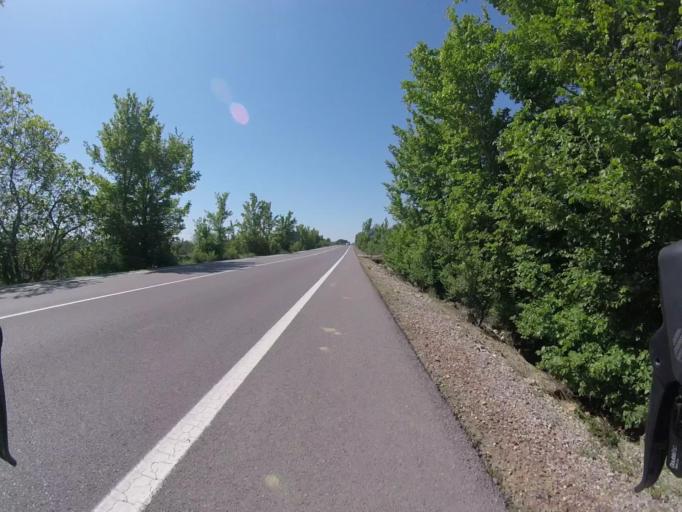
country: ES
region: Valencia
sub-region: Provincia de Castello
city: Benlloch
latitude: 40.2260
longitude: 0.0519
